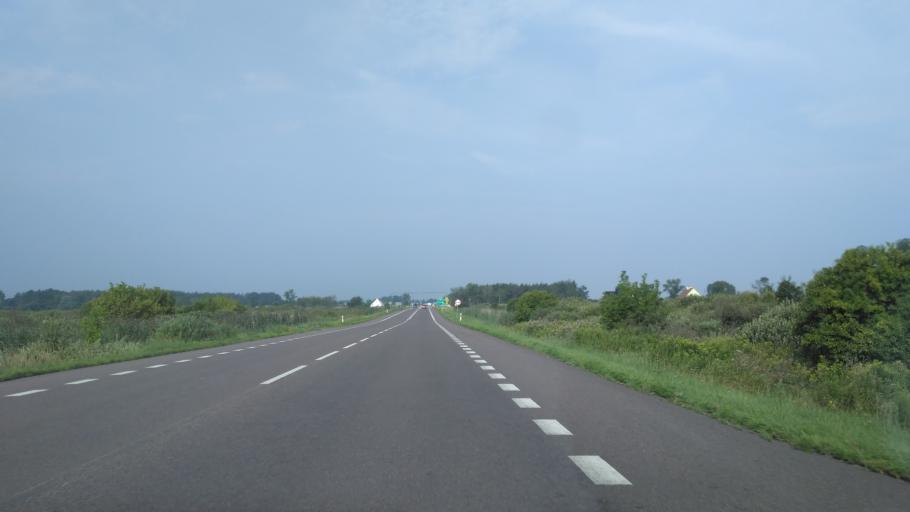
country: PL
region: Lublin Voivodeship
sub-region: Powiat swidnicki
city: Trawniki
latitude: 51.1639
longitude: 23.0380
